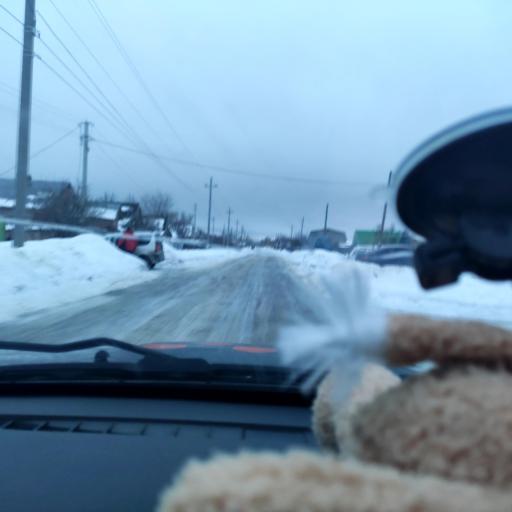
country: RU
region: Samara
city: Tol'yatti
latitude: 53.5742
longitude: 49.3243
